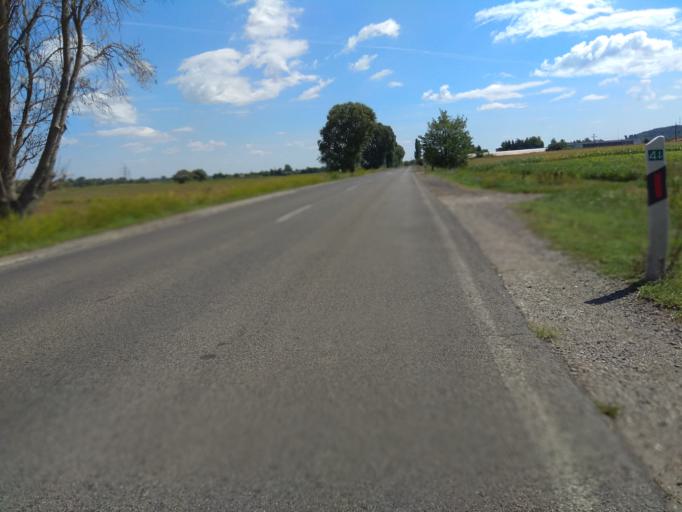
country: HU
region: Borsod-Abauj-Zemplen
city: Sajokaza
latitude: 48.2656
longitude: 20.6038
